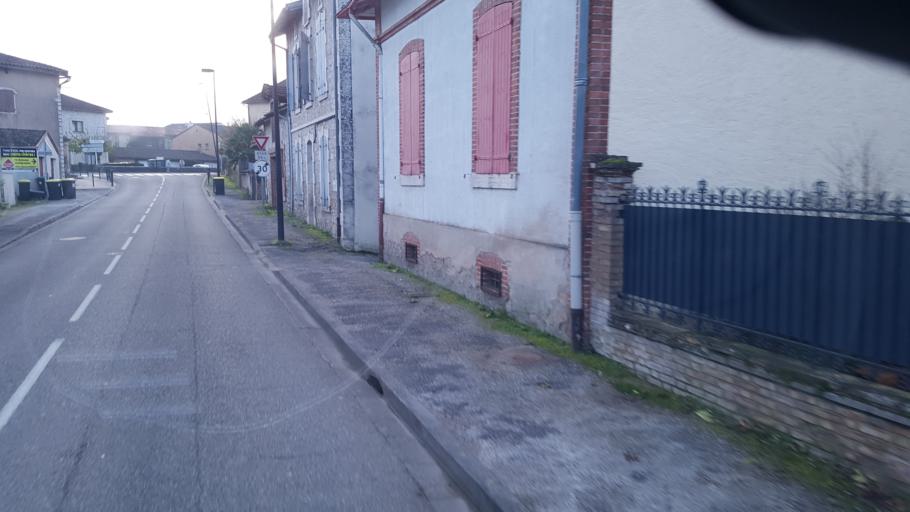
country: FR
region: Midi-Pyrenees
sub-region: Departement du Tarn-et-Garonne
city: Caussade
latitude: 44.1645
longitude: 1.5355
